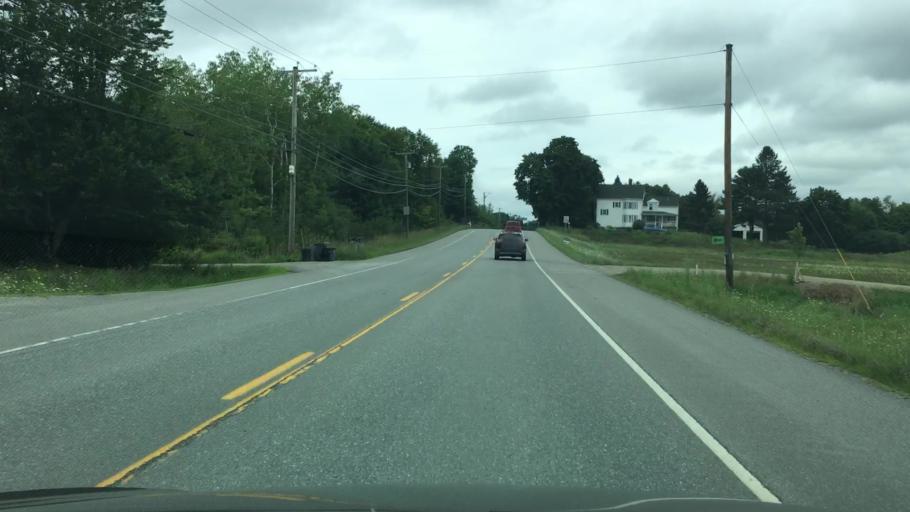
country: US
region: Maine
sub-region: Penobscot County
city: Orrington
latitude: 44.7099
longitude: -68.8252
